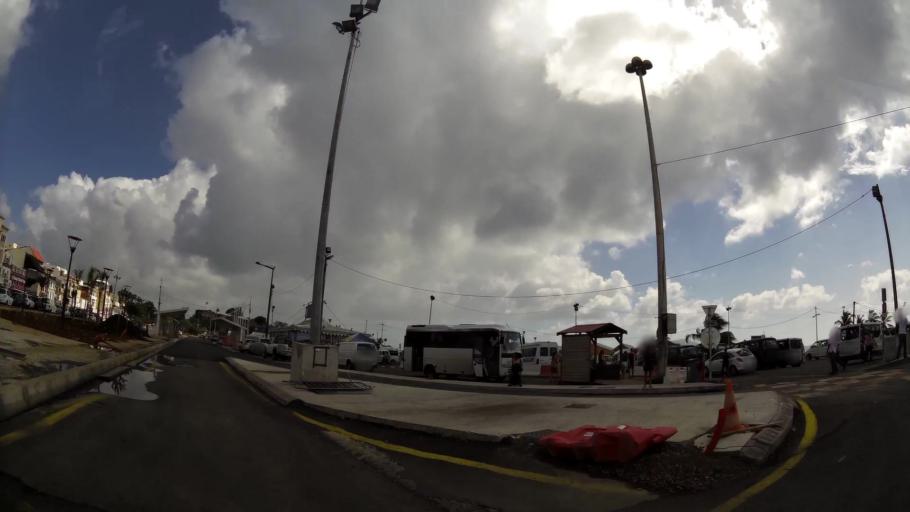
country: MQ
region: Martinique
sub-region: Martinique
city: Fort-de-France
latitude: 14.6034
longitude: -61.0712
